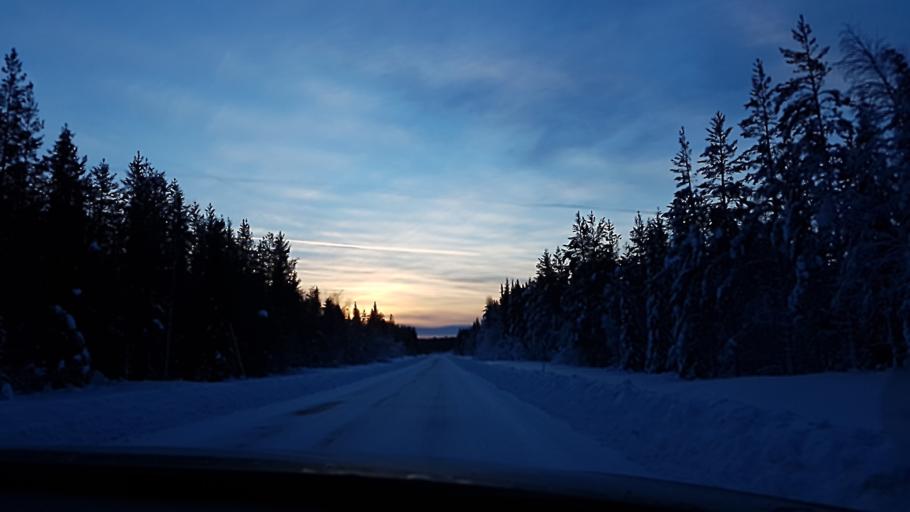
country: SE
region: Norrbotten
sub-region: Jokkmokks Kommun
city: Jokkmokk
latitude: 66.0892
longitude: 20.0711
